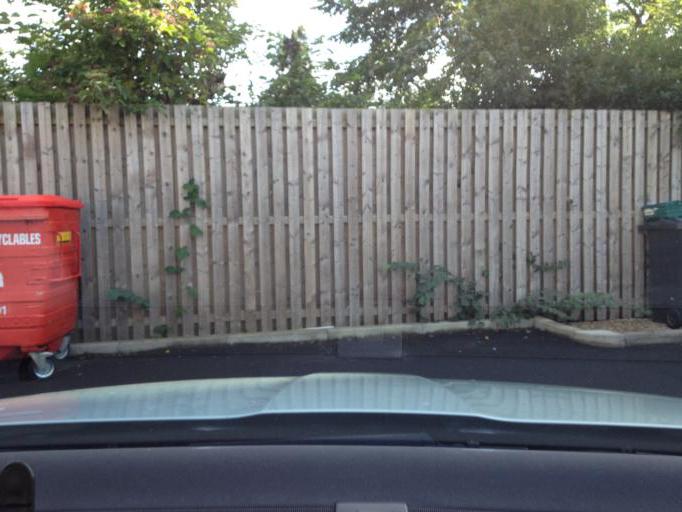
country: GB
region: Scotland
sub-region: West Lothian
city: East Calder
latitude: 55.8949
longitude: -3.4652
